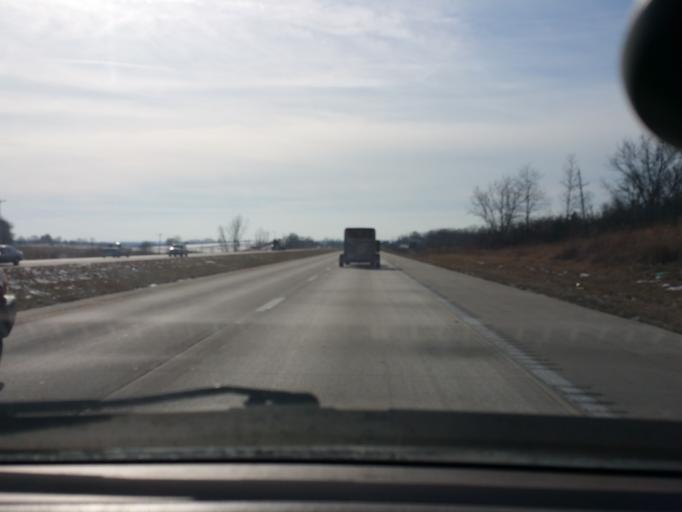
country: US
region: Missouri
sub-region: Clay County
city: Kearney
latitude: 39.4341
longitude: -94.3362
